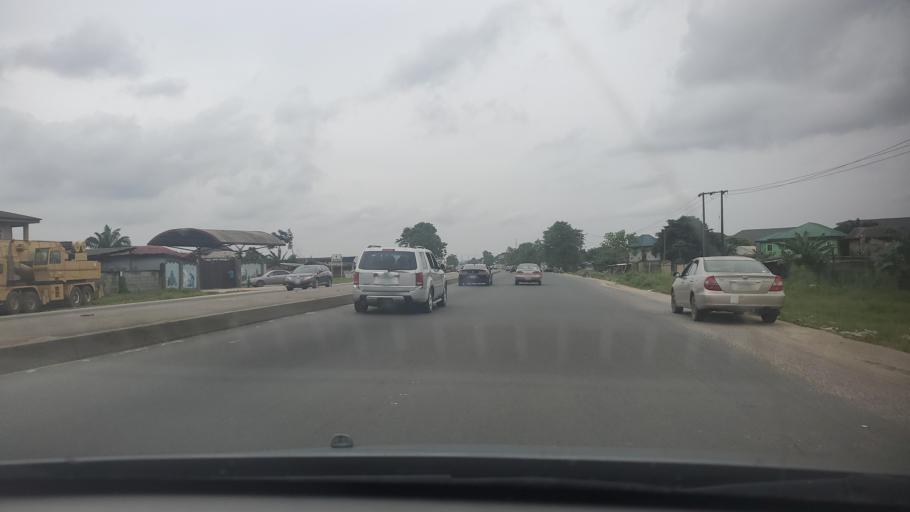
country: NG
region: Rivers
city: Emuoha
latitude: 4.8714
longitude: 6.9646
